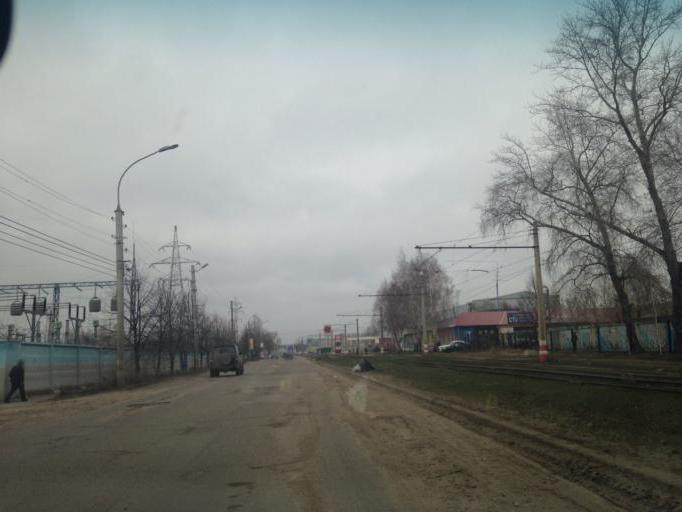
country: RU
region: Ulyanovsk
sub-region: Ulyanovskiy Rayon
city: Ulyanovsk
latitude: 54.2928
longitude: 48.2934
